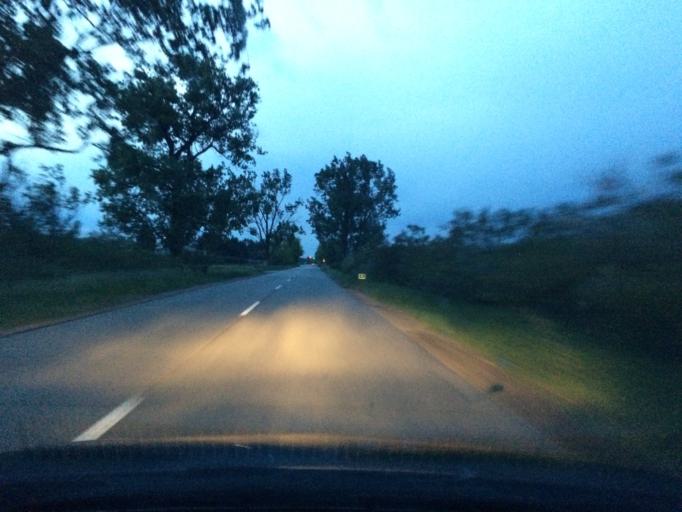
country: HU
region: Szabolcs-Szatmar-Bereg
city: Tiszavasvari
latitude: 47.9265
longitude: 21.3883
